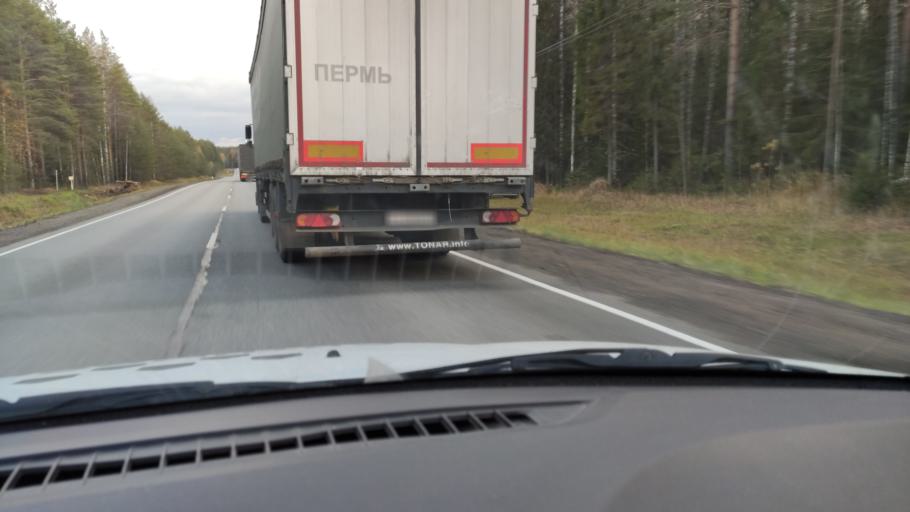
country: RU
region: Kirov
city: Dubrovka
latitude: 58.9085
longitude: 51.1791
